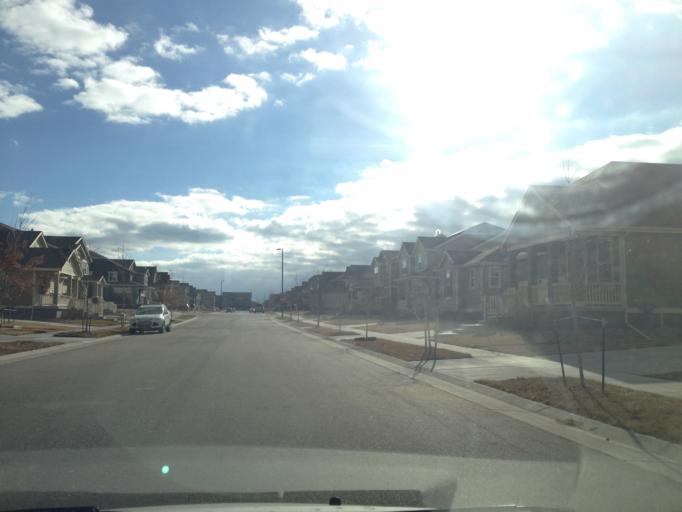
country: US
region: Colorado
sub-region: Boulder County
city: Lafayette
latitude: 40.0329
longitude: -105.0888
